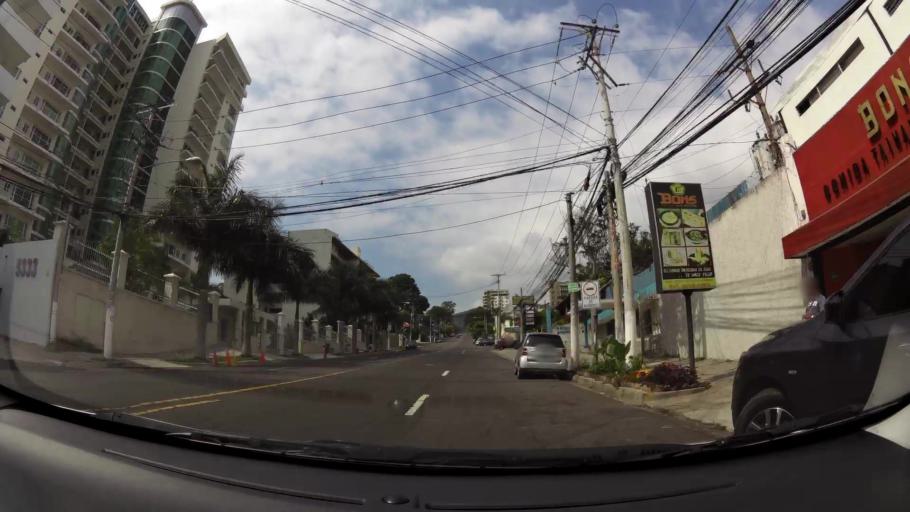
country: SV
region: La Libertad
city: Santa Tecla
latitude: 13.7039
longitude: -89.2522
